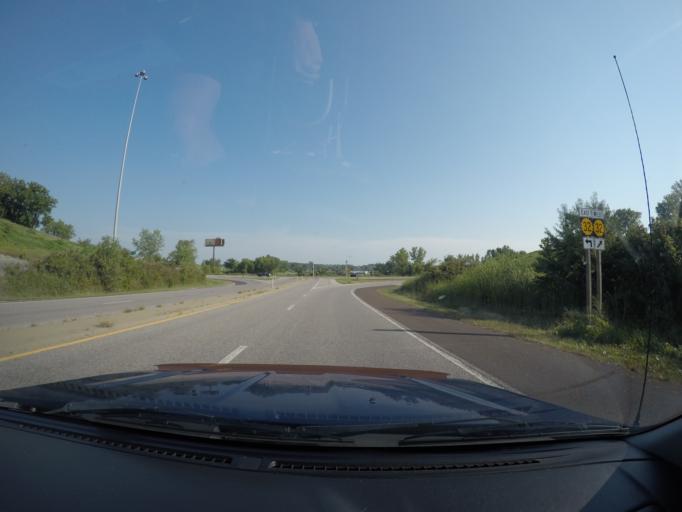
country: US
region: Kansas
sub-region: Wyandotte County
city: Edwardsville
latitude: 39.0627
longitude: -94.7943
